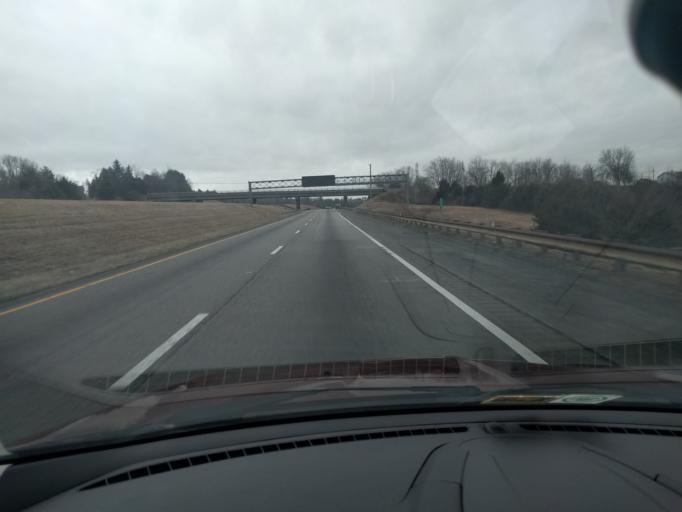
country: US
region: Virginia
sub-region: Augusta County
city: Verona
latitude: 38.1500
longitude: -79.0174
